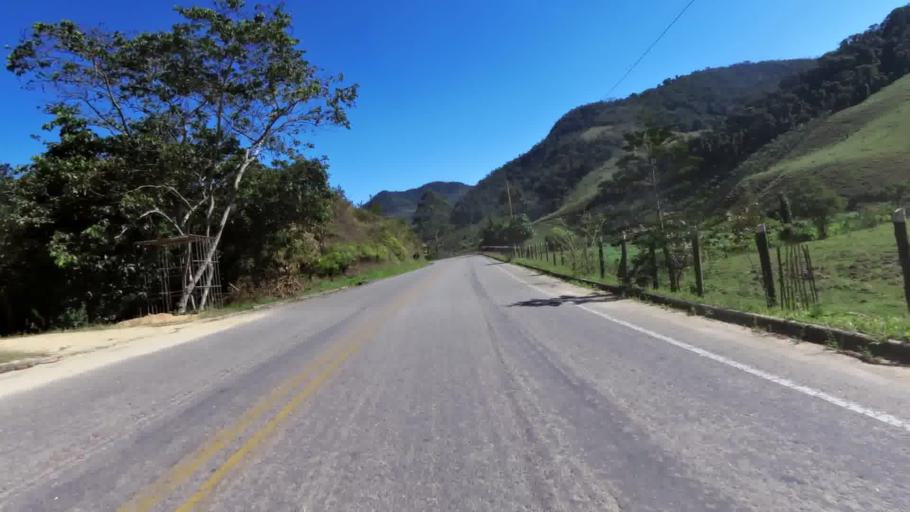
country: BR
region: Espirito Santo
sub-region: Vargem Alta
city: Vargem Alta
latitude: -20.7129
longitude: -40.9127
